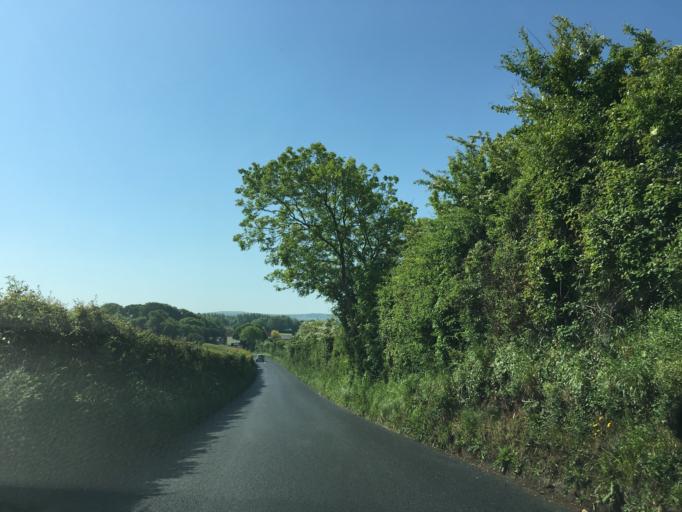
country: GB
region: England
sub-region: Isle of Wight
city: Newchurch
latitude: 50.6570
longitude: -1.2118
